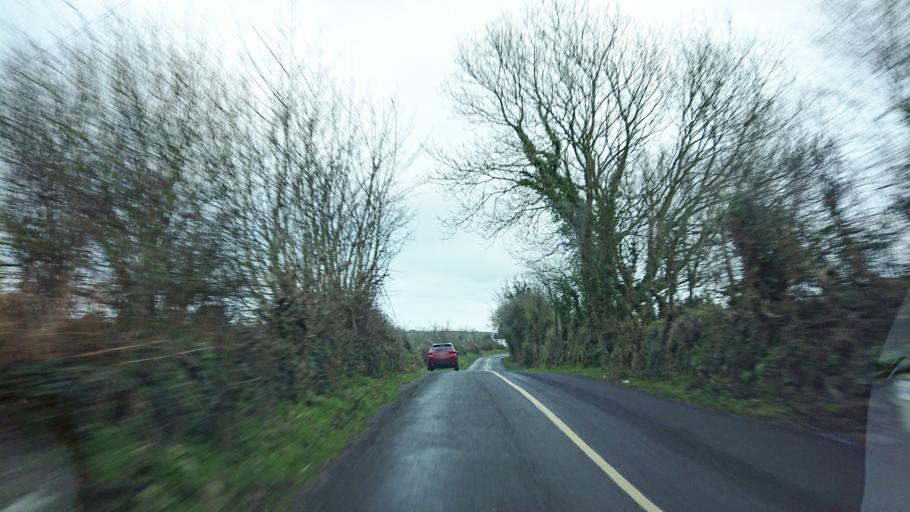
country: IE
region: Munster
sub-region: Waterford
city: Portlaw
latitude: 52.1702
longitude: -7.3945
